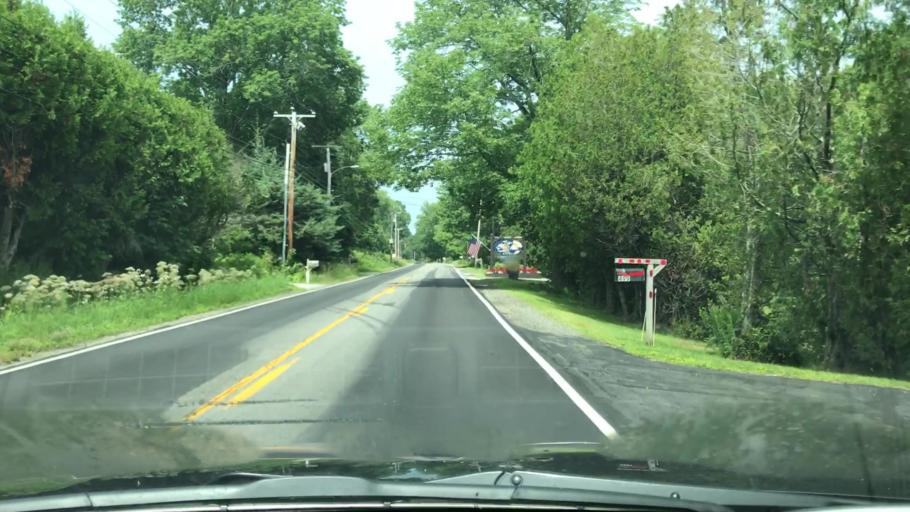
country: US
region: Maine
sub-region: Knox County
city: Camden
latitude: 44.2425
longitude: -69.0370
